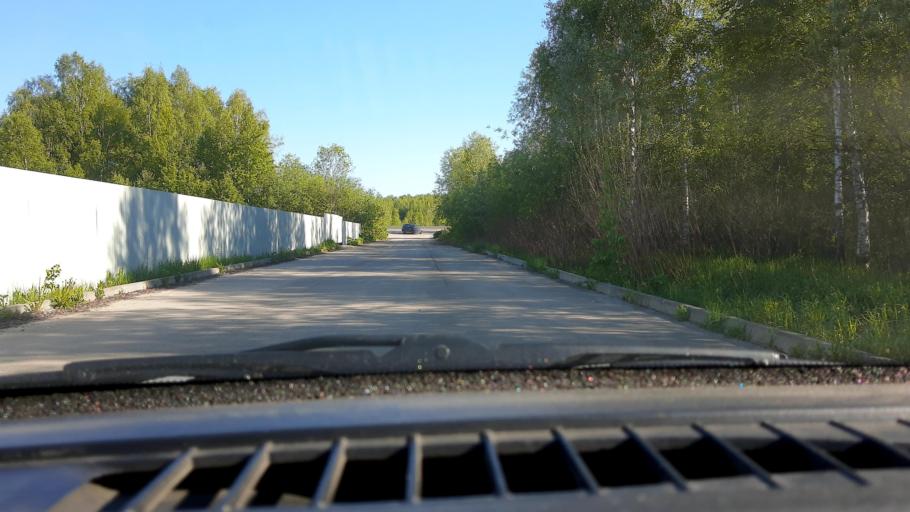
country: RU
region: Nizjnij Novgorod
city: Gorbatovka
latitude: 56.3090
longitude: 43.7844
